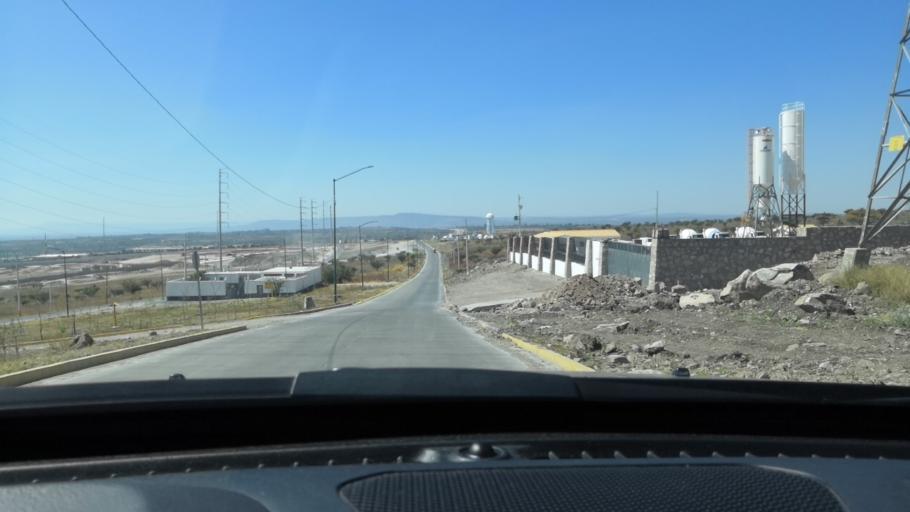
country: MX
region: Guanajuato
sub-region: Leon
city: Centro Familiar la Soledad
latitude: 21.1141
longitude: -101.7526
